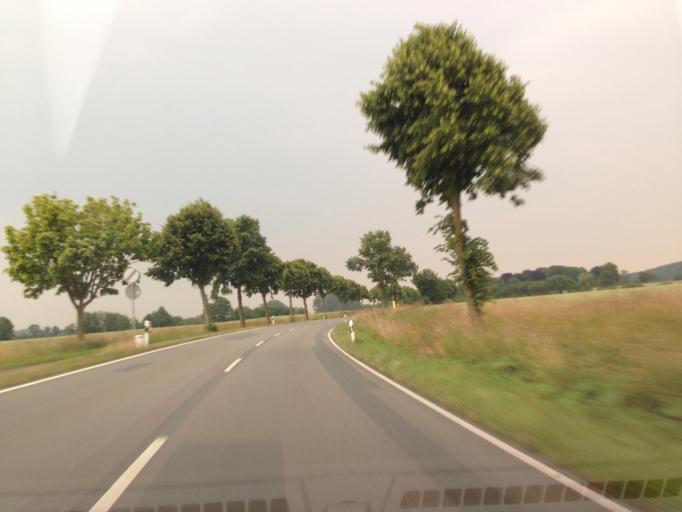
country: DE
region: North Rhine-Westphalia
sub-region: Regierungsbezirk Munster
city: Havixbeck
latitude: 51.9630
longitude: 7.4245
